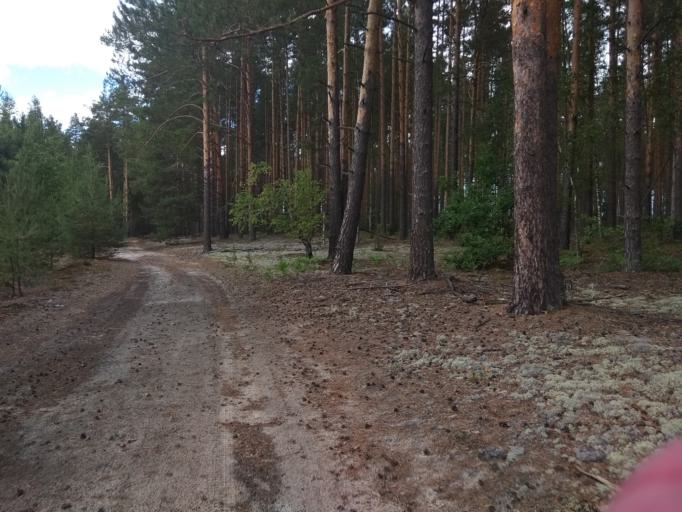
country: RU
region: Moskovskaya
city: Misheronskiy
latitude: 55.6410
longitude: 39.7033
